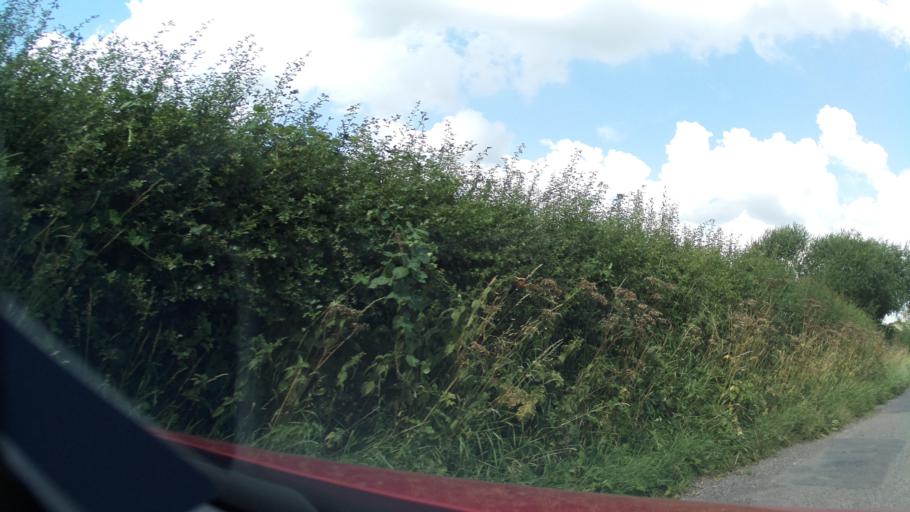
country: GB
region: England
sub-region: Wiltshire
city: Hankerton
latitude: 51.5897
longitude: -2.0218
